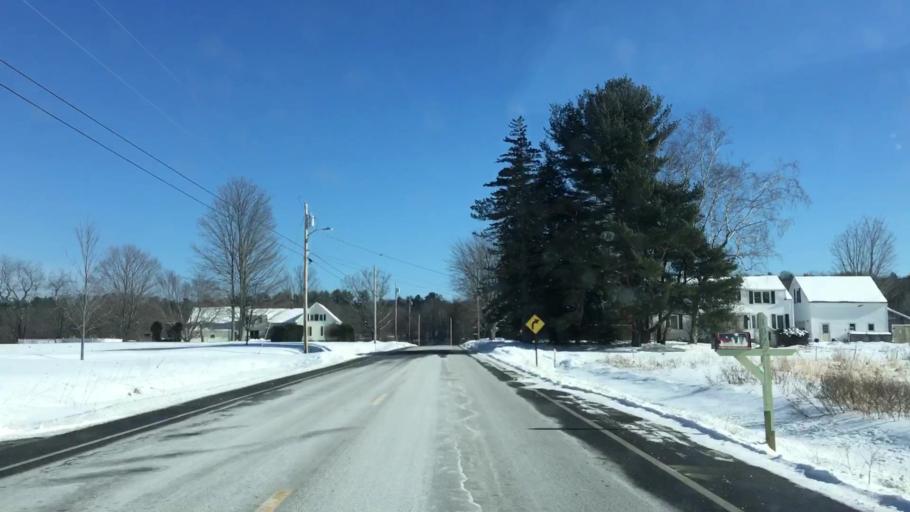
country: US
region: Maine
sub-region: Androscoggin County
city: Lisbon
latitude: 44.0296
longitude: -70.0848
